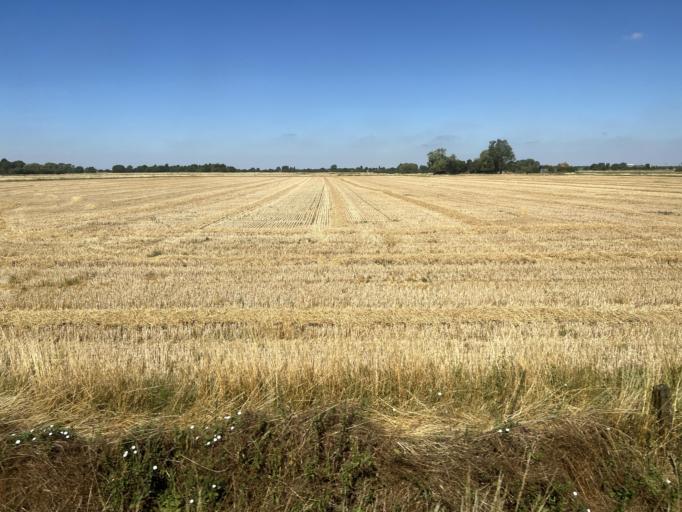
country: GB
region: England
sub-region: Lincolnshire
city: Boston
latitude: 53.0098
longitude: -0.0060
